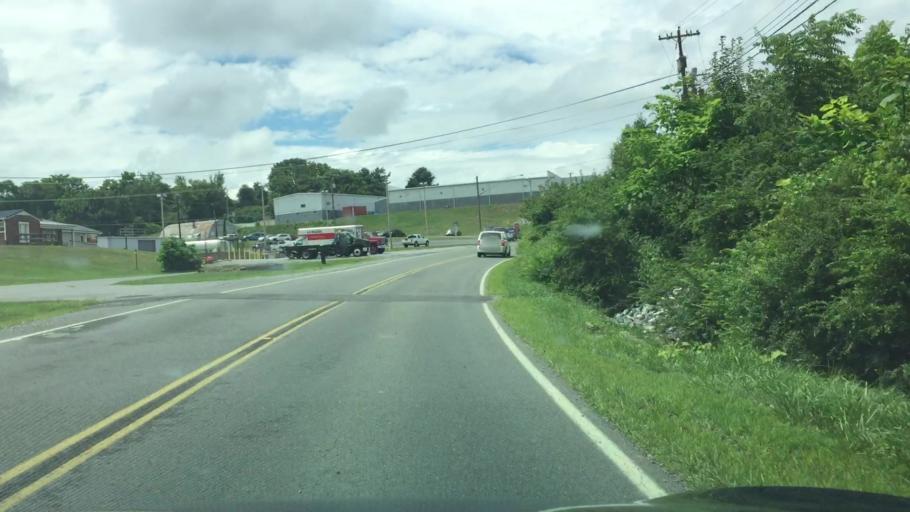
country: US
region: Virginia
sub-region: Wythe County
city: Wytheville
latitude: 36.9481
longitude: -81.0649
